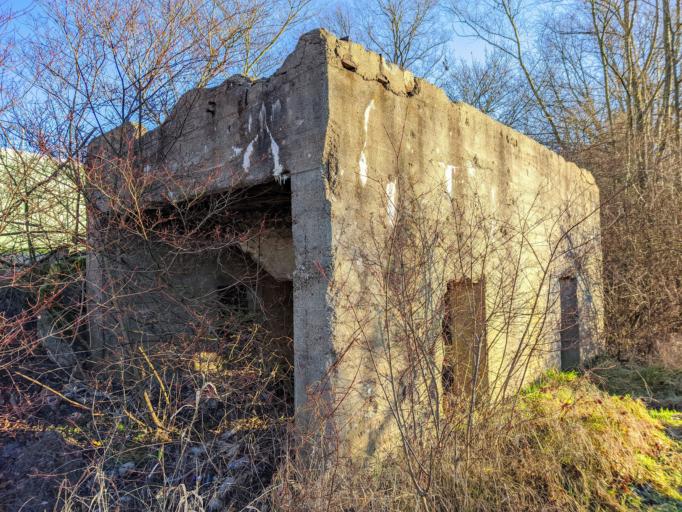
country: PL
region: Lubusz
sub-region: Powiat zielonogorski
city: Nowogrod Bobrzanski
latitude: 51.8078
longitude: 15.2387
